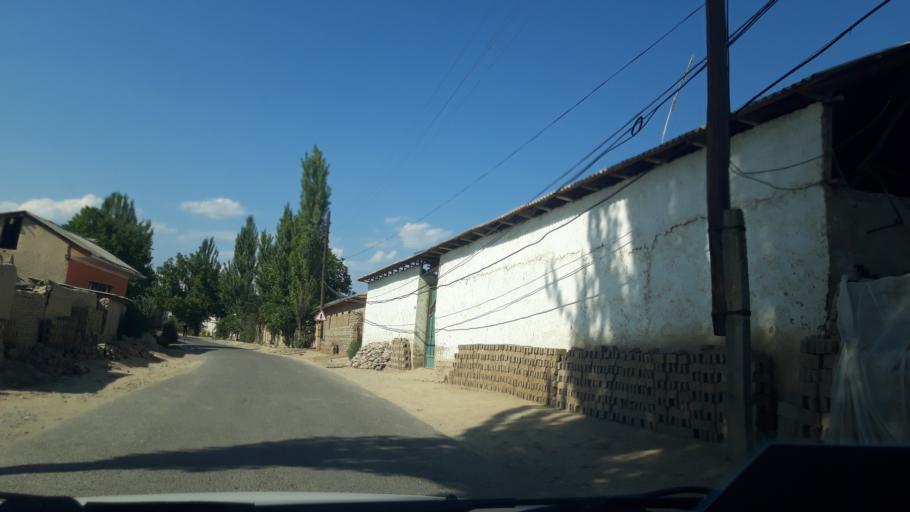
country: UZ
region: Namangan
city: Yangiqo`rg`on
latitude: 41.2041
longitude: 71.7262
